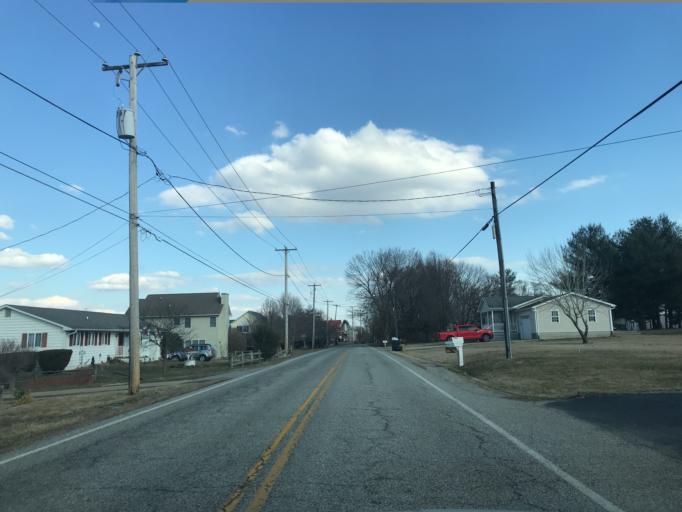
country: US
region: Maryland
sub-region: Cecil County
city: North East
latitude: 39.6451
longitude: -75.9647
